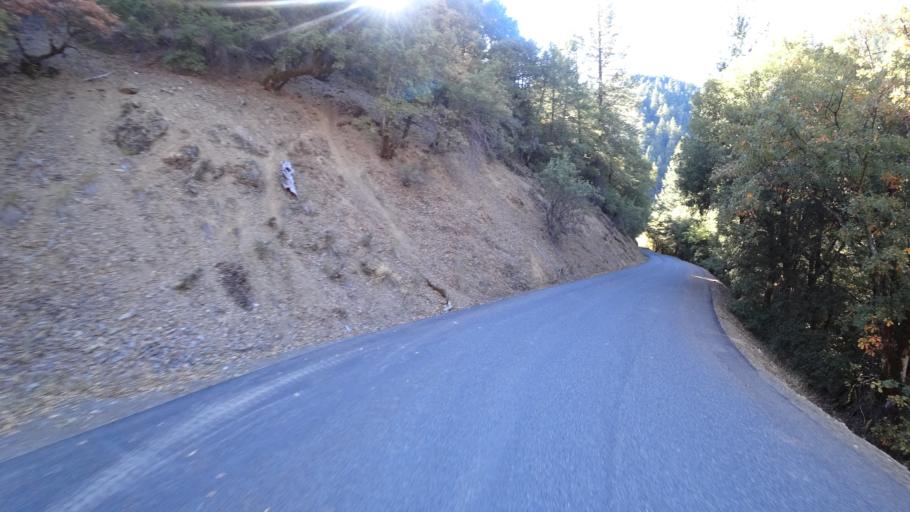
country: US
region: California
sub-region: Humboldt County
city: Willow Creek
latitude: 41.1669
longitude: -123.2140
